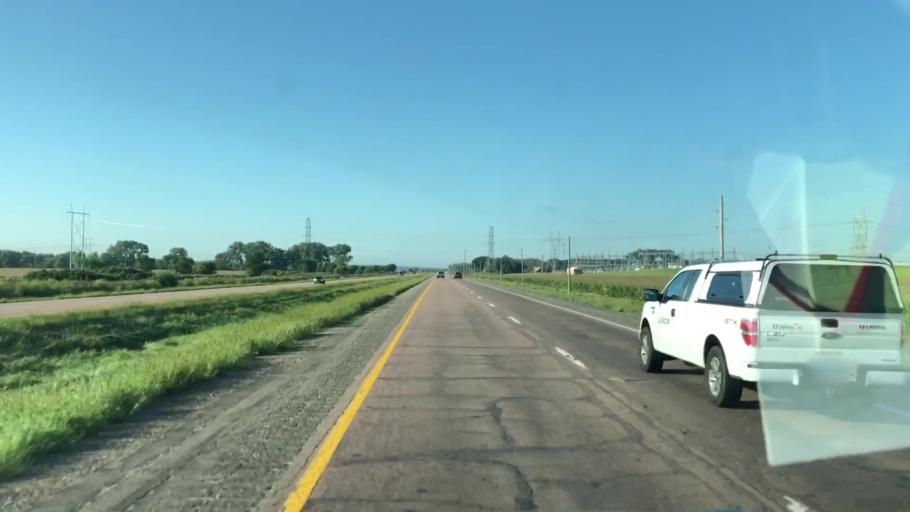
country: US
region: Iowa
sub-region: Woodbury County
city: Sioux City
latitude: 42.6062
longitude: -96.2993
